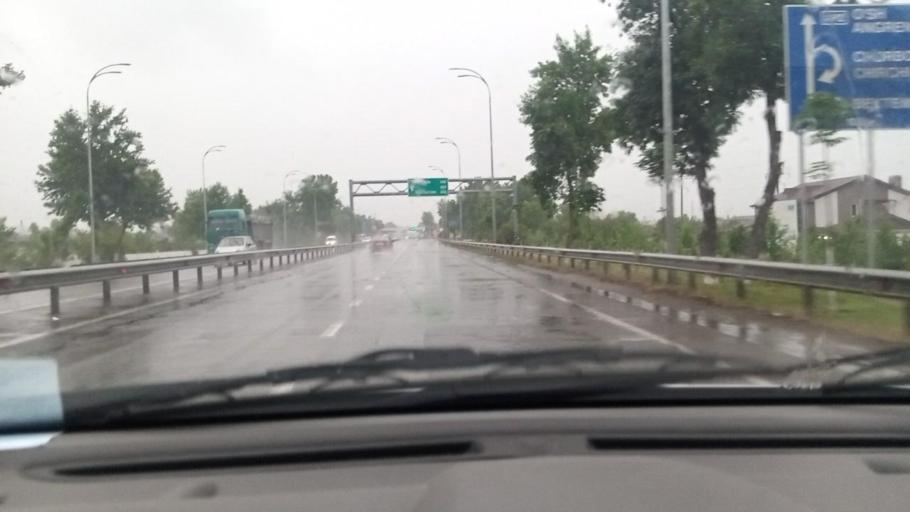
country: UZ
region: Toshkent Shahri
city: Bektemir
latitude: 41.2512
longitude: 69.3876
